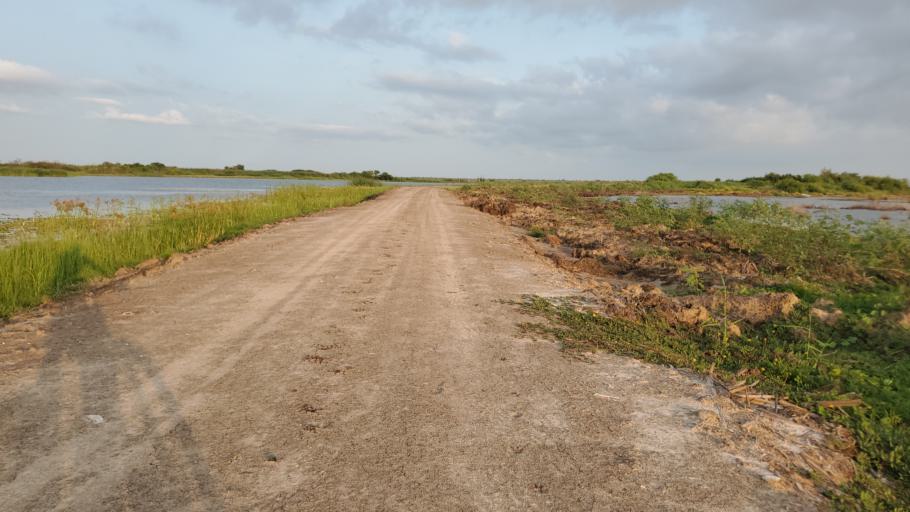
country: SN
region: Saint-Louis
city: Saint-Louis
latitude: 16.0180
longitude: -16.4026
